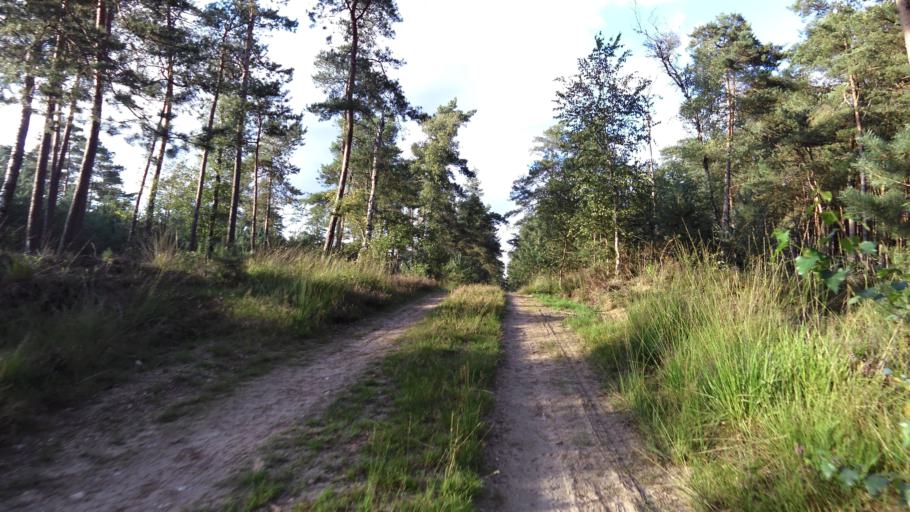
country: NL
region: Gelderland
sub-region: Gemeente Epe
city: Vaassen
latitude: 52.2752
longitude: 5.8831
